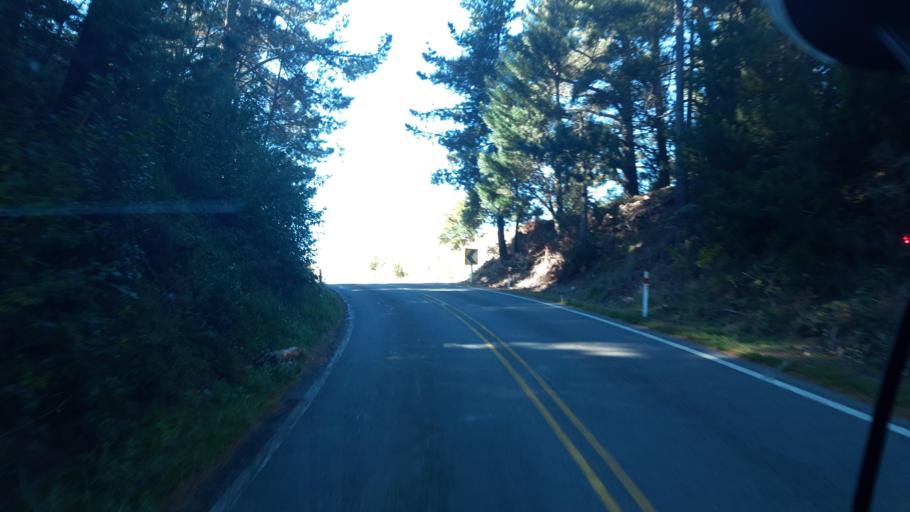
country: NZ
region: Canterbury
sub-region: Waimakariri District
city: Oxford
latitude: -43.2257
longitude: 172.2913
